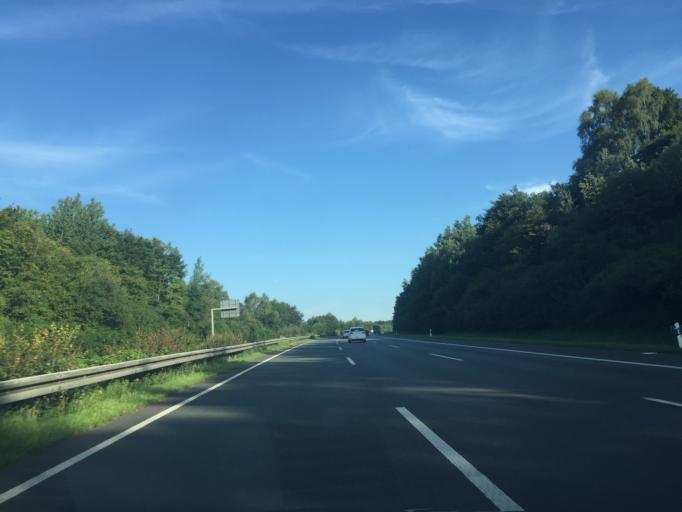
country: DE
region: North Rhine-Westphalia
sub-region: Regierungsbezirk Arnsberg
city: Drolshagen
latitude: 51.0393
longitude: 7.8055
